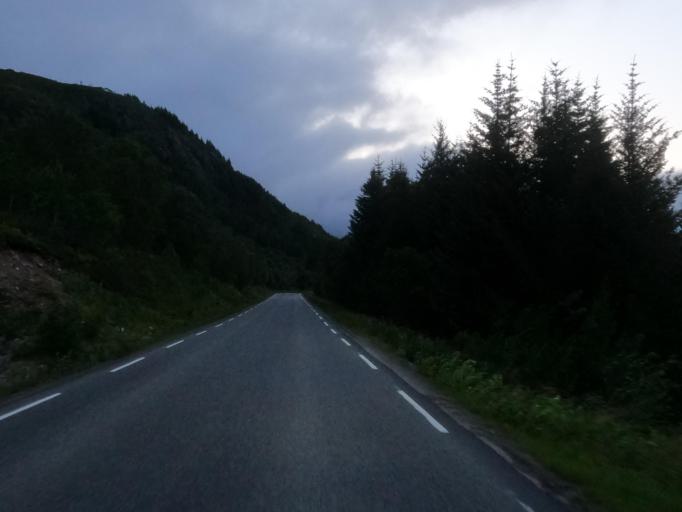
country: NO
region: Nordland
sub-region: Lodingen
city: Lodingen
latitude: 68.5928
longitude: 15.7894
